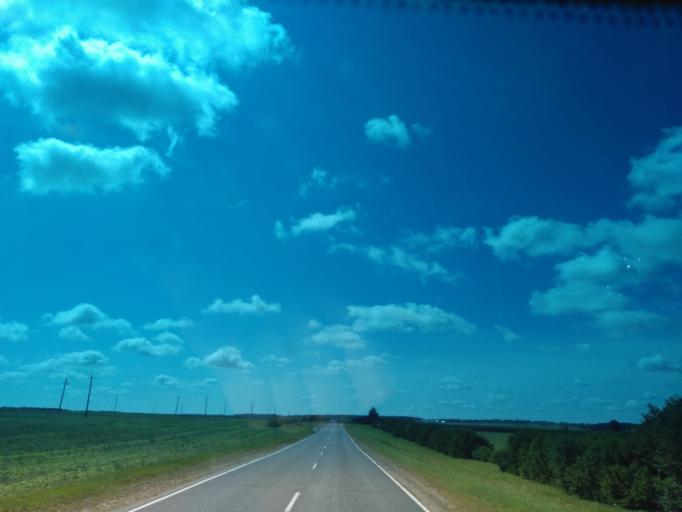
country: BY
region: Minsk
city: Uzda
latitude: 53.3783
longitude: 27.2379
